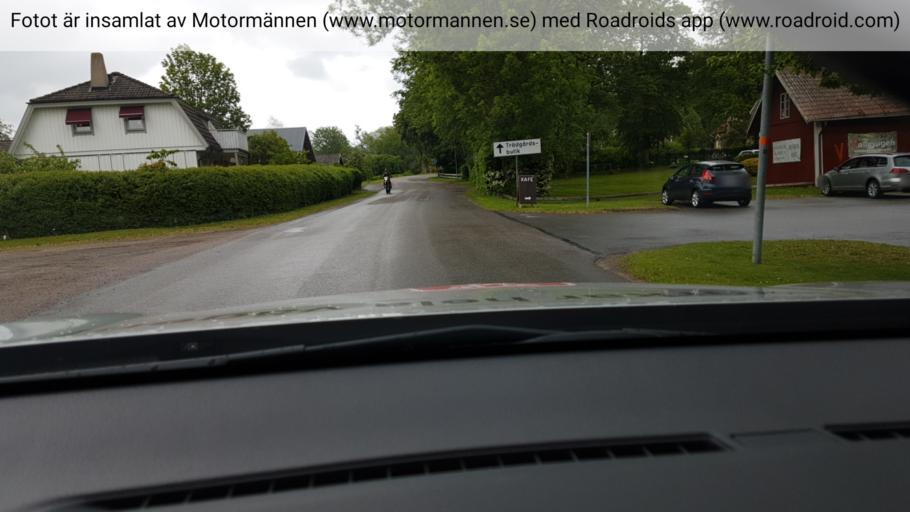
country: SE
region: Vaestra Goetaland
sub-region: Skara Kommun
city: Axvall
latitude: 58.3861
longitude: 13.6531
